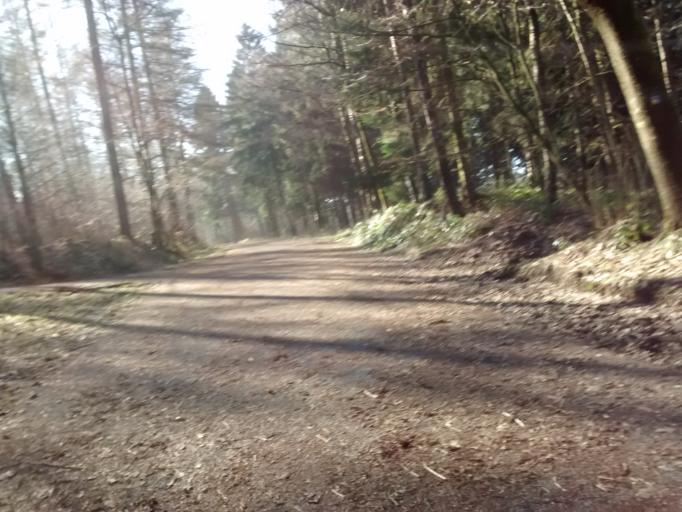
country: NL
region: Limburg
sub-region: Gemeente Vaals
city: Vaals
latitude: 50.7491
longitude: 6.0439
